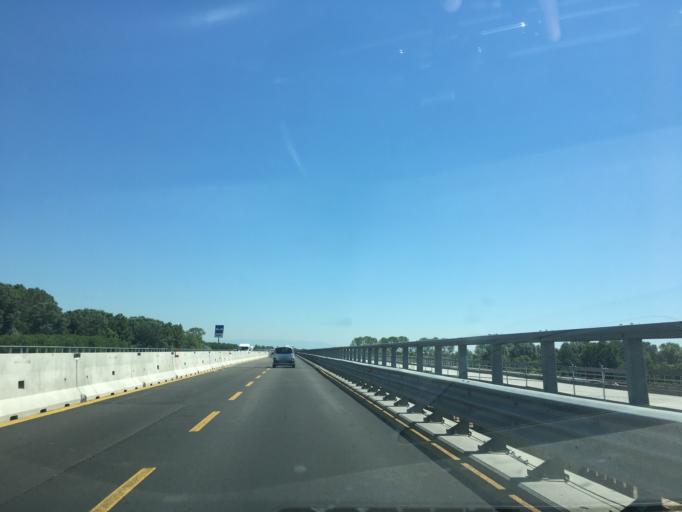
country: IT
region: Friuli Venezia Giulia
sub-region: Provincia di Udine
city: Ronchis
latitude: 45.8137
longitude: 12.9875
